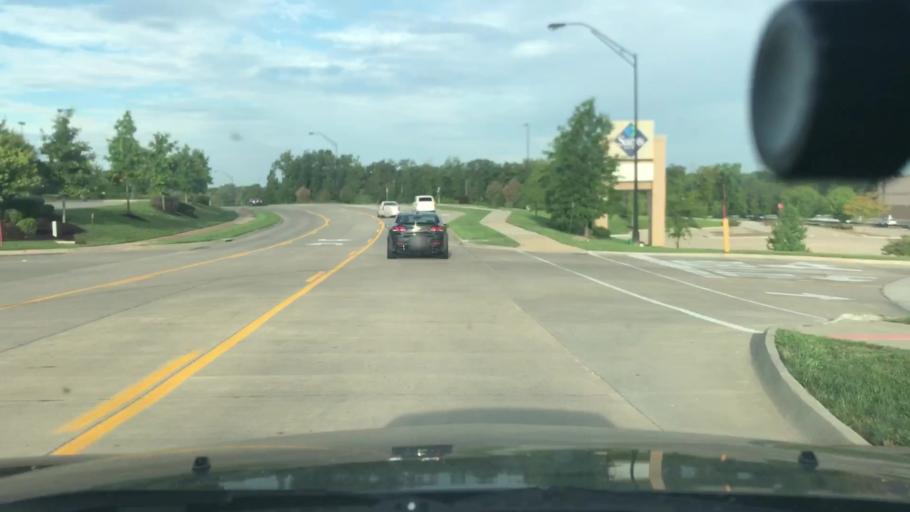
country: US
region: Missouri
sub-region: Saint Charles County
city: Wentzville
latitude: 38.8130
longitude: -90.8794
